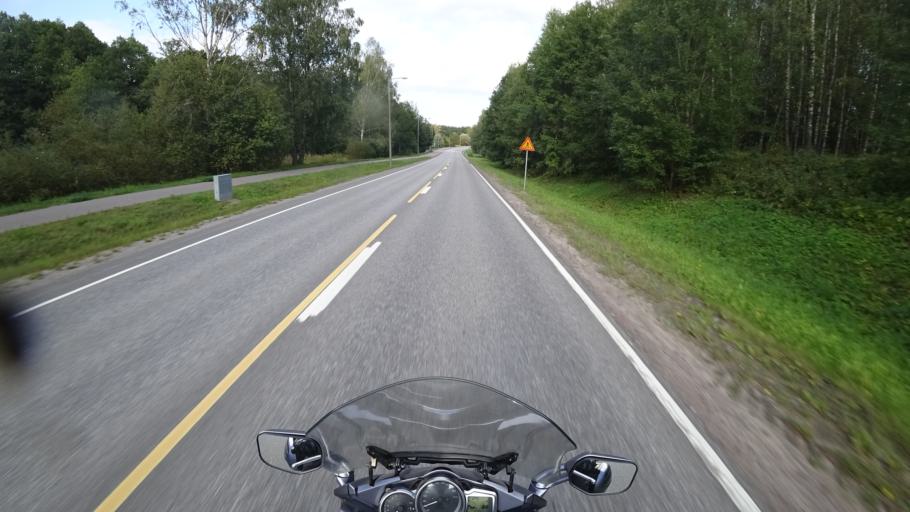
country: FI
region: Uusimaa
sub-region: Raaseporin
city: Pohja
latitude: 60.1029
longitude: 23.5544
